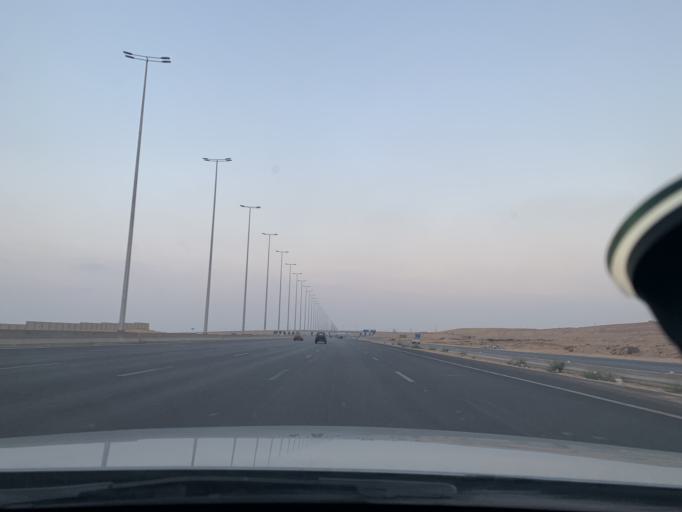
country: EG
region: Muhafazat al Qalyubiyah
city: Al Khankah
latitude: 30.0925
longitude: 31.4967
